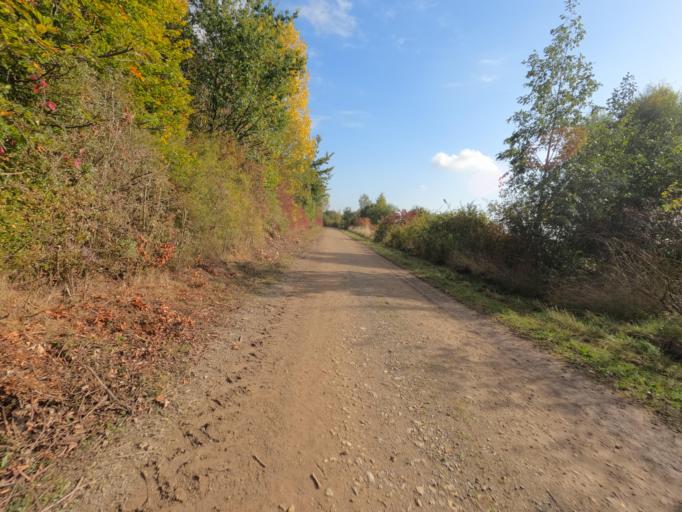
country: DE
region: North Rhine-Westphalia
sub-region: Regierungsbezirk Koln
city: Inden
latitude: 50.8526
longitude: 6.3428
